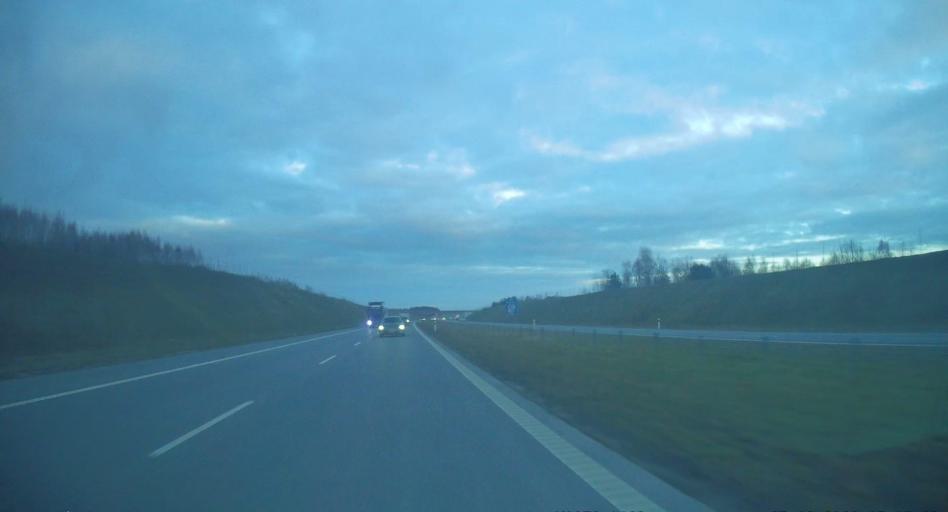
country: PL
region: Silesian Voivodeship
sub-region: Powiat klobucki
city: Kamyk
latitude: 50.8736
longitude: 19.1030
